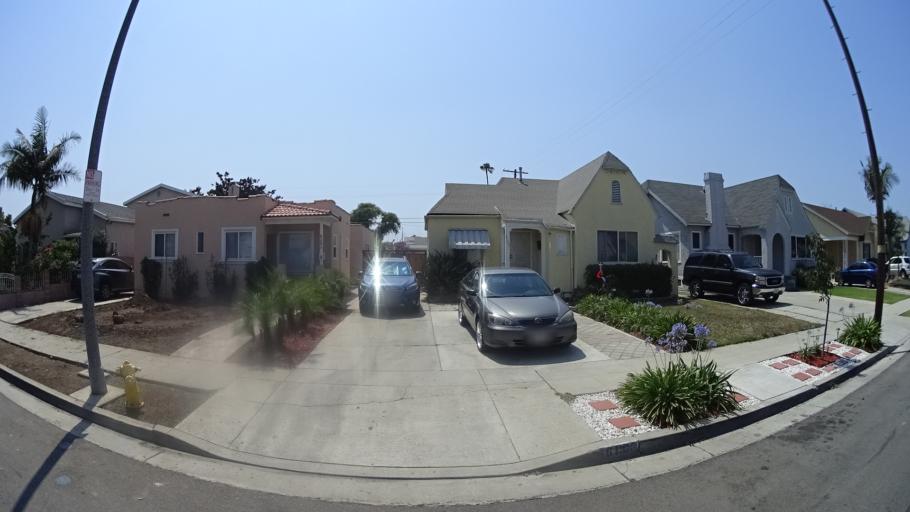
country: US
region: California
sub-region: Los Angeles County
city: View Park-Windsor Hills
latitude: 33.9837
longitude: -118.3407
